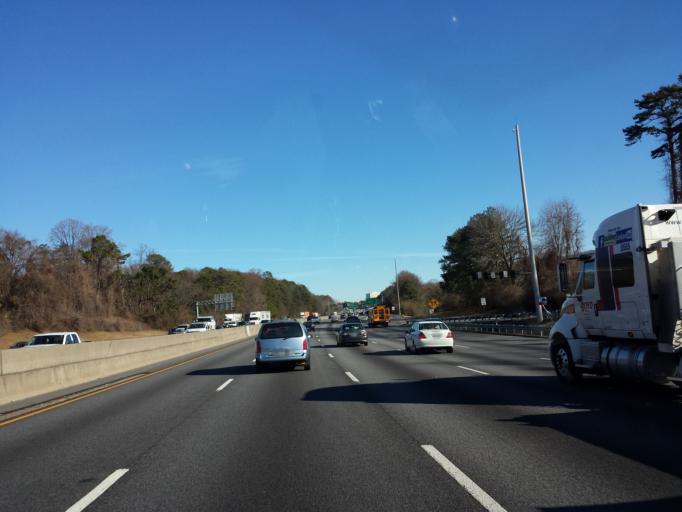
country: US
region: Georgia
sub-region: Fulton County
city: Sandy Springs
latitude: 33.9121
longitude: -84.3768
